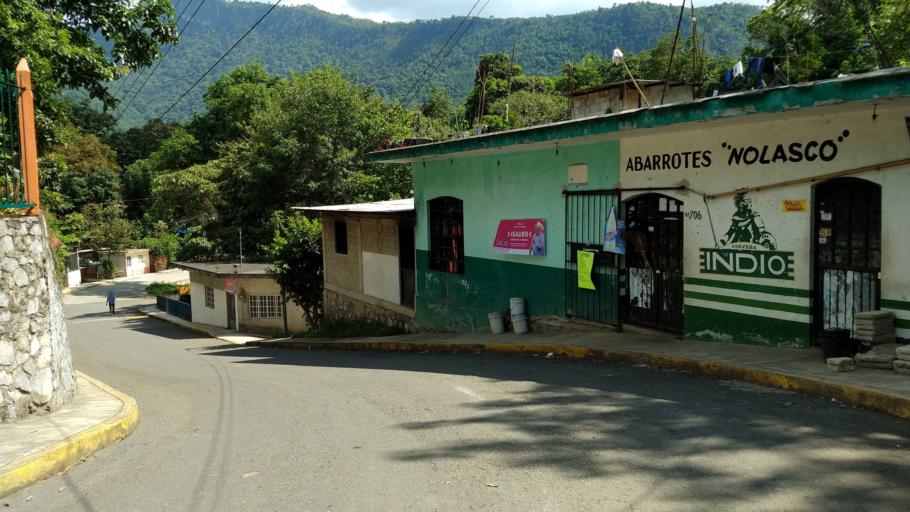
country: MX
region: Veracruz
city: Jalapilla
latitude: 18.8125
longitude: -97.0695
